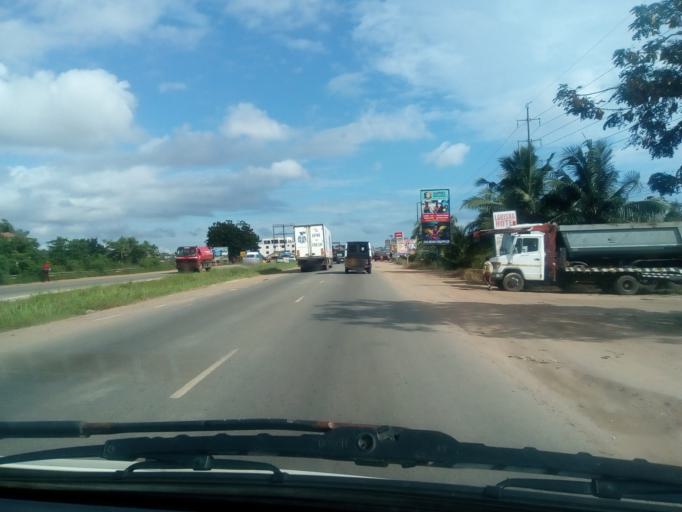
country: GH
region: Greater Accra
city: Achiaman
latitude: 5.6997
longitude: -0.2935
